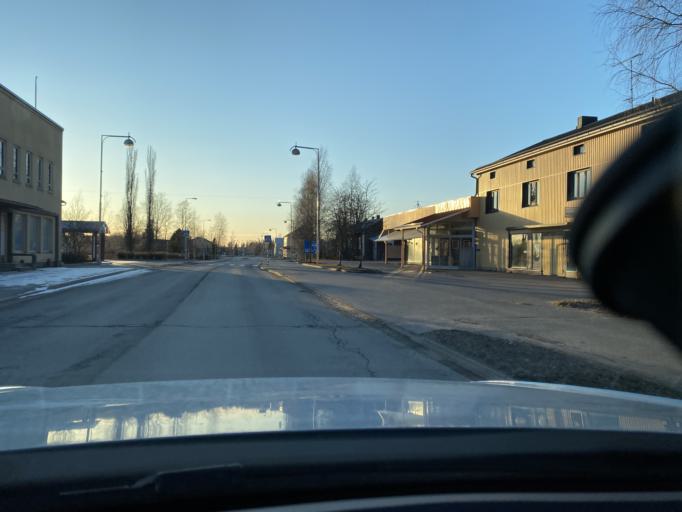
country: FI
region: Pirkanmaa
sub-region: Lounais-Pirkanmaa
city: Punkalaidun
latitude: 61.1109
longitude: 23.1113
